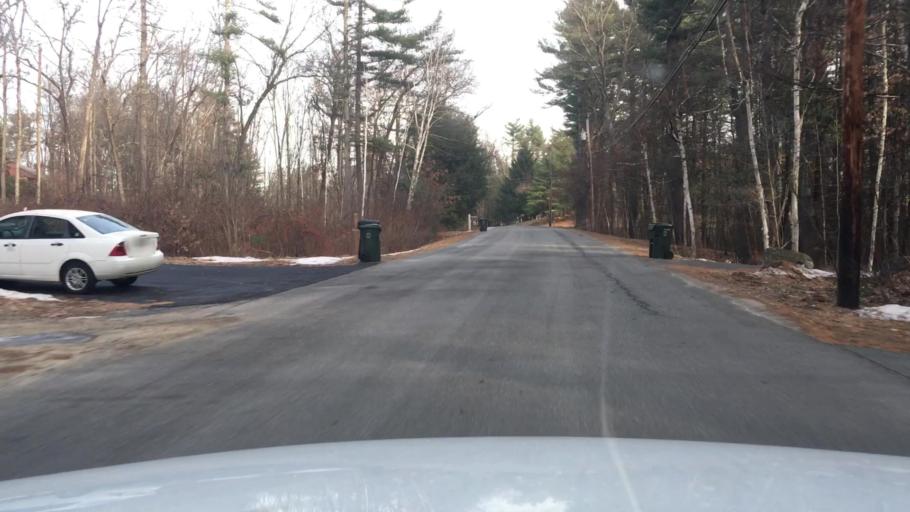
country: US
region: New Hampshire
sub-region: Rockingham County
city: Londonderry
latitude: 42.8853
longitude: -71.4154
